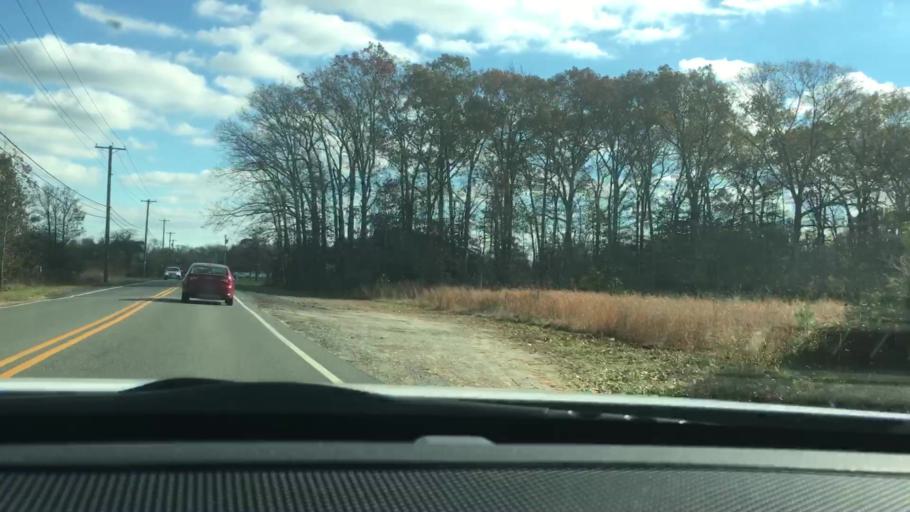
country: US
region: New Jersey
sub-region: Atlantic County
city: Northfield
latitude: 39.3786
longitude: -74.5758
